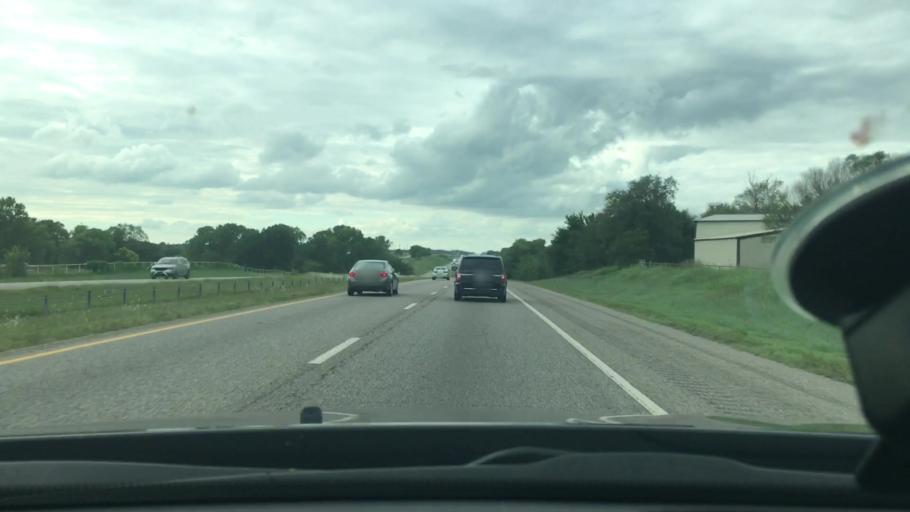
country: US
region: Oklahoma
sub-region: Cleveland County
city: Noble
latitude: 35.1098
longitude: -97.4365
